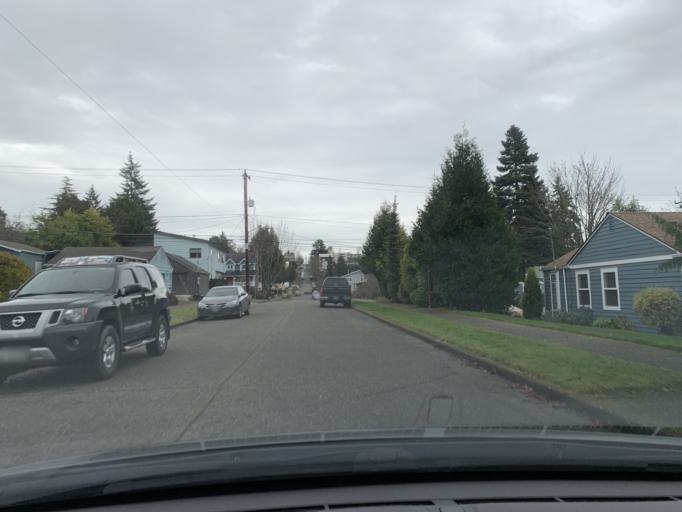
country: US
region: Washington
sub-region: King County
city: White Center
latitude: 47.5630
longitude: -122.3948
